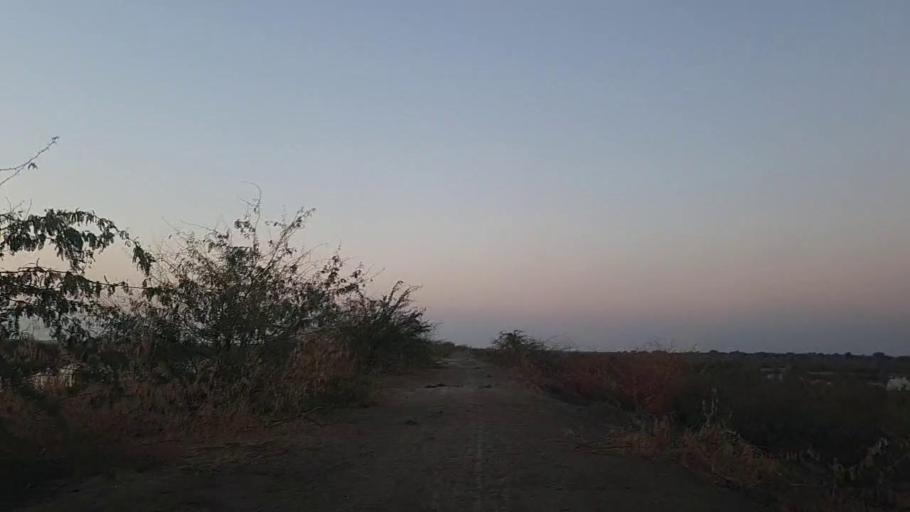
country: PK
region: Sindh
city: Tando Mittha Khan
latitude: 26.0775
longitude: 69.1533
